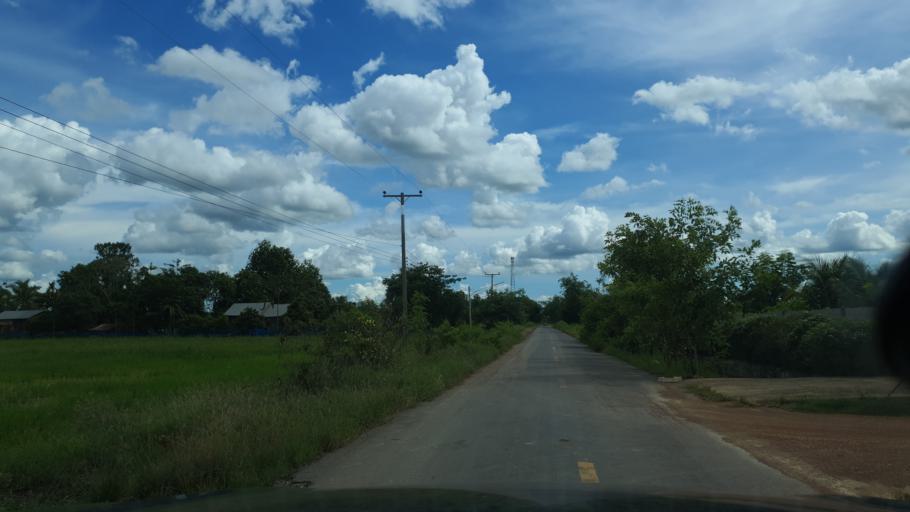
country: TH
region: Sukhothai
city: Thung Saliam
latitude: 17.3348
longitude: 99.6324
